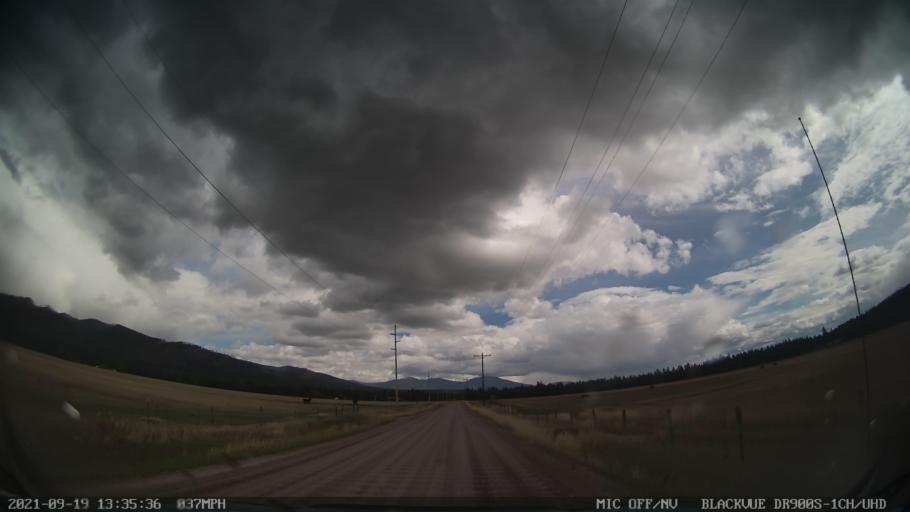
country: US
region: Montana
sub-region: Missoula County
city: Seeley Lake
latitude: 47.1066
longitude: -113.3095
